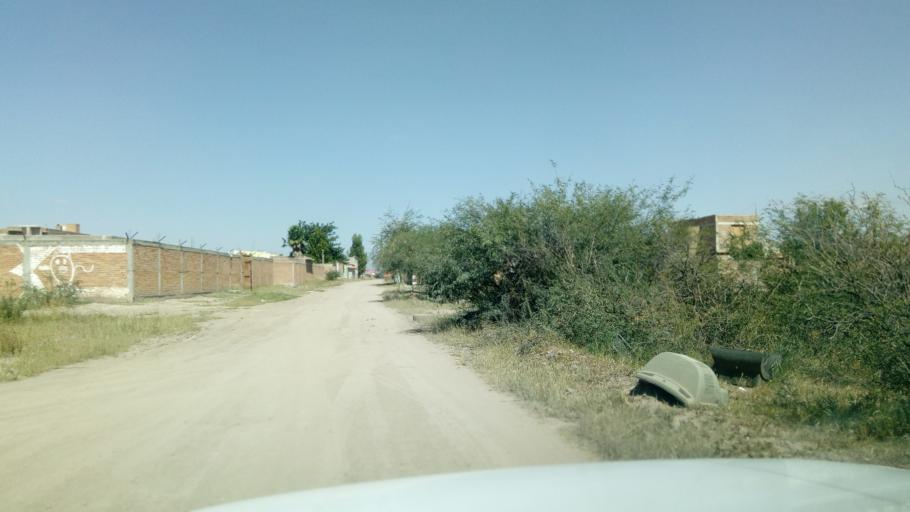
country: MX
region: Durango
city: Victoria de Durango
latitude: 23.9826
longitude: -104.6825
